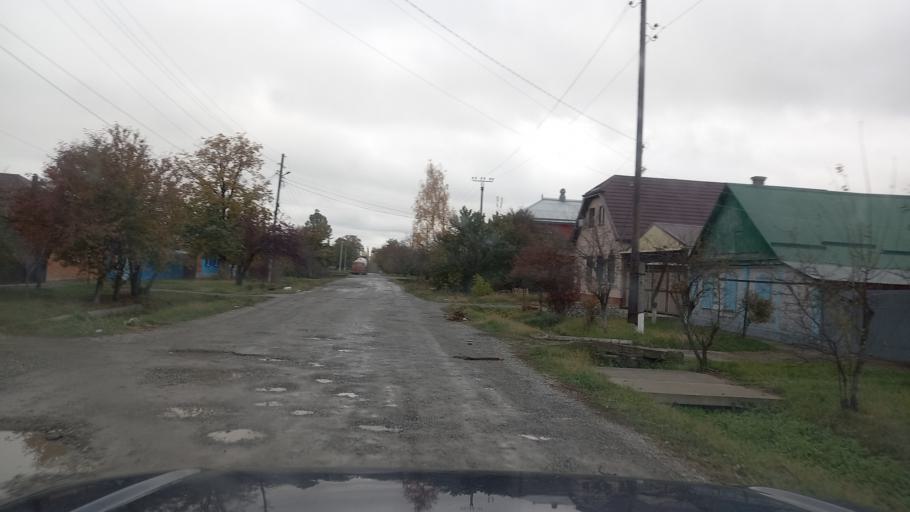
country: RU
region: Adygeya
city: Maykop
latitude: 44.6158
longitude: 40.1281
